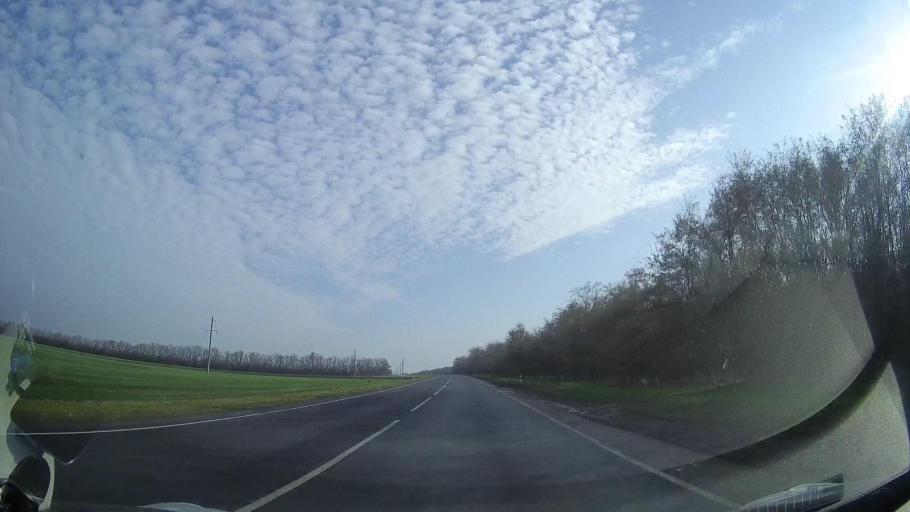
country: RU
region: Rostov
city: Gigant
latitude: 46.5292
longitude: 41.1939
